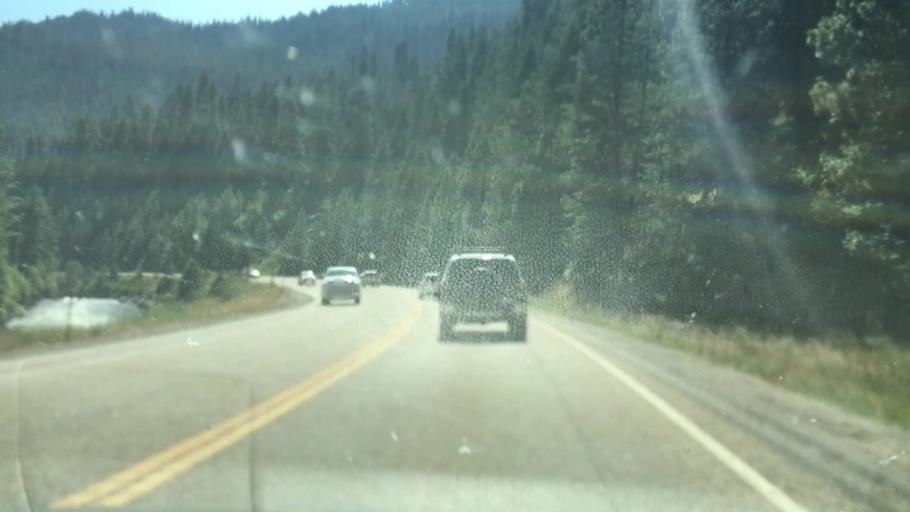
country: US
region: Idaho
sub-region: Valley County
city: Cascade
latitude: 44.1776
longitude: -116.1164
